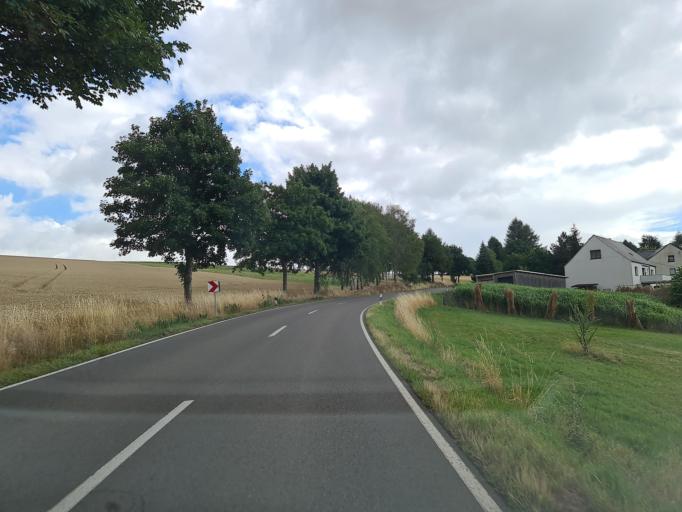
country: DE
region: Saxony
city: Grosshartmannsdorf
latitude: 50.7815
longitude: 13.2854
